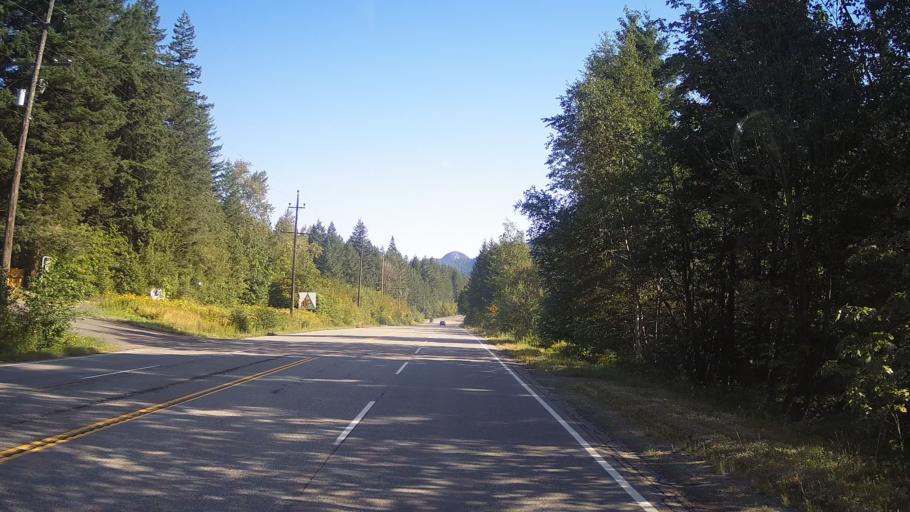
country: CA
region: British Columbia
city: Hope
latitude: 49.4975
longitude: -121.4202
